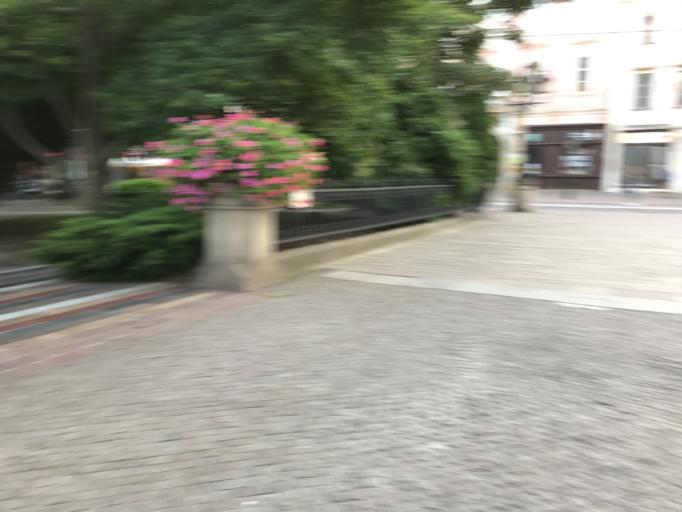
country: SK
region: Kosicky
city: Kosice
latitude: 48.7214
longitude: 21.2575
